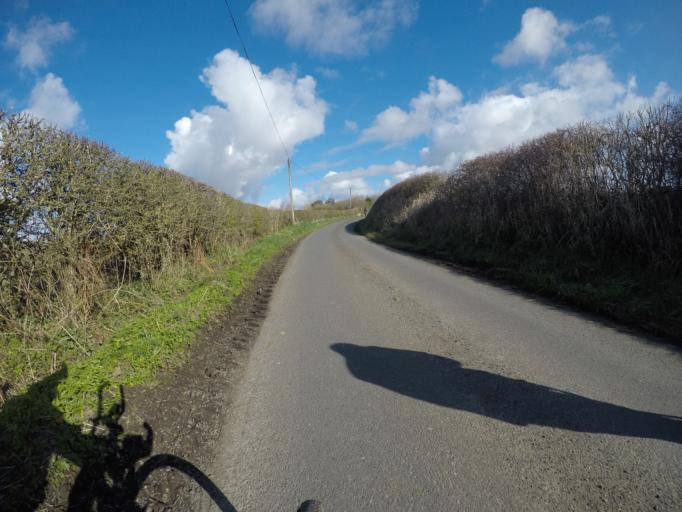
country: GB
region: Scotland
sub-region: North Ayrshire
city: Irvine
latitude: 55.6567
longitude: -4.6547
